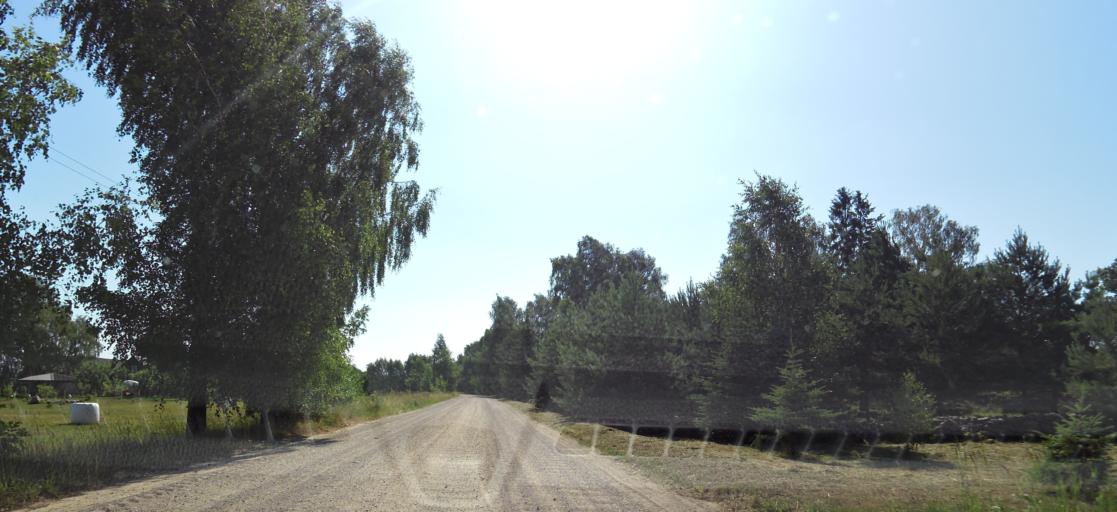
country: LT
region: Panevezys
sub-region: Birzai
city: Birzai
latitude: 56.2457
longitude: 24.8792
